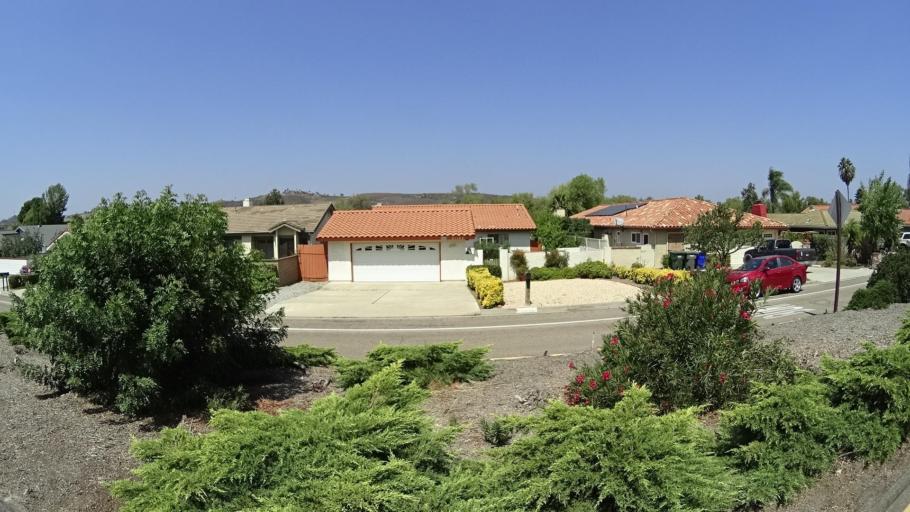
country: US
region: California
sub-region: San Diego County
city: Bonsall
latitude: 33.2797
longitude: -117.2207
